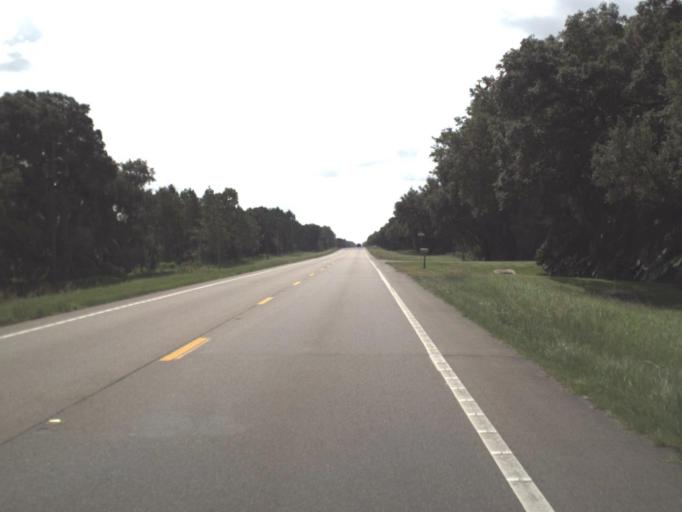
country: US
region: Florida
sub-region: Pasco County
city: Zephyrhills North
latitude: 28.2900
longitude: -82.1309
